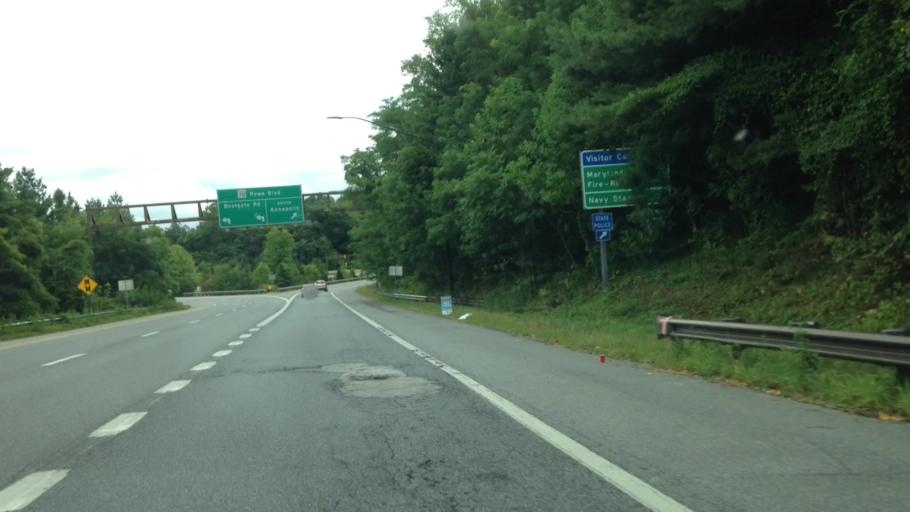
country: US
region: Maryland
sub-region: Anne Arundel County
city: Parole
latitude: 38.9932
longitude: -76.5163
